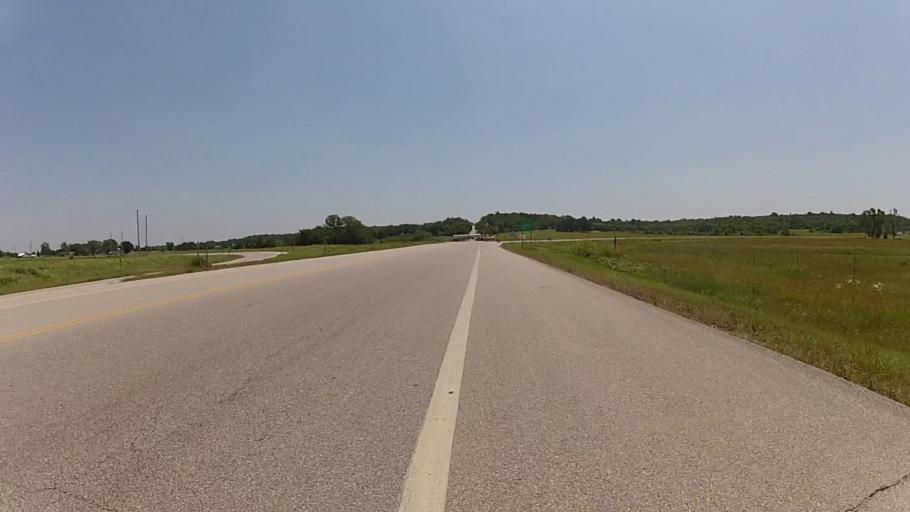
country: US
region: Kansas
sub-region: Montgomery County
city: Cherryvale
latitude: 37.2238
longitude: -95.5881
